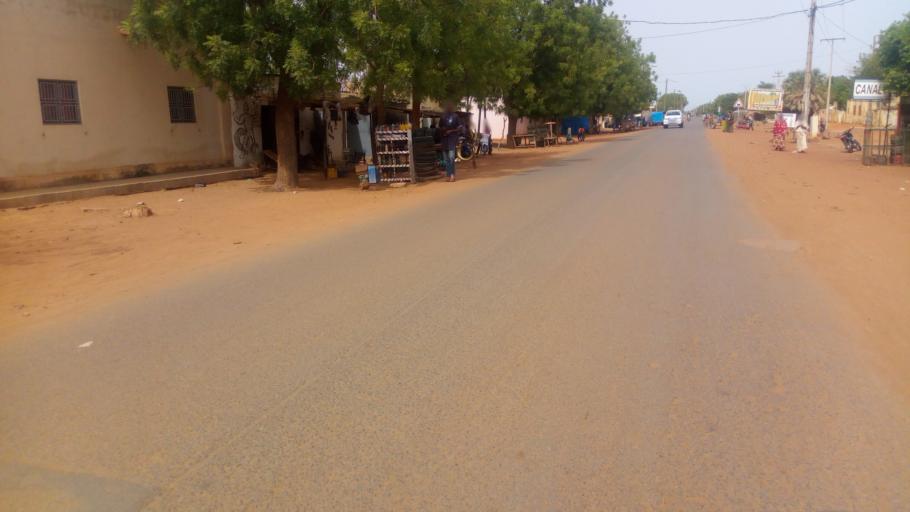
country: ML
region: Segou
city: Segou
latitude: 13.4339
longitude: -6.2925
